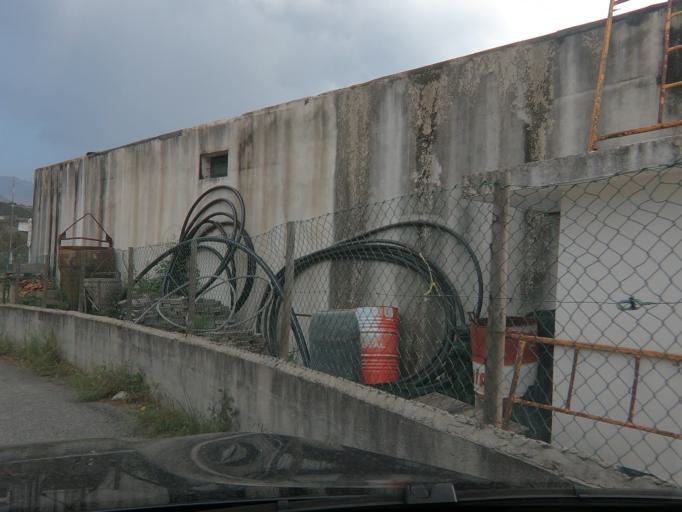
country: PT
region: Vila Real
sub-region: Vila Real
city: Vila Real
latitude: 41.3082
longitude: -7.6967
